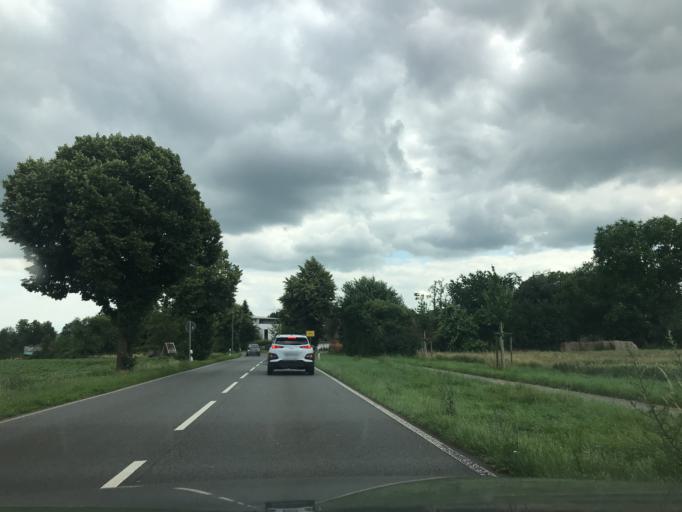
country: DE
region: North Rhine-Westphalia
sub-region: Regierungsbezirk Dusseldorf
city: Neubrueck
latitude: 51.1421
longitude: 6.6793
